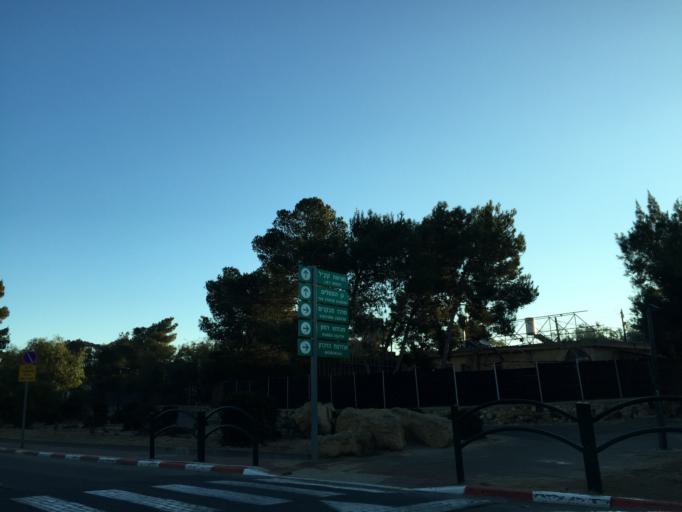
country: IL
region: Southern District
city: Mitzpe Ramon
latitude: 30.6112
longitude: 34.8025
